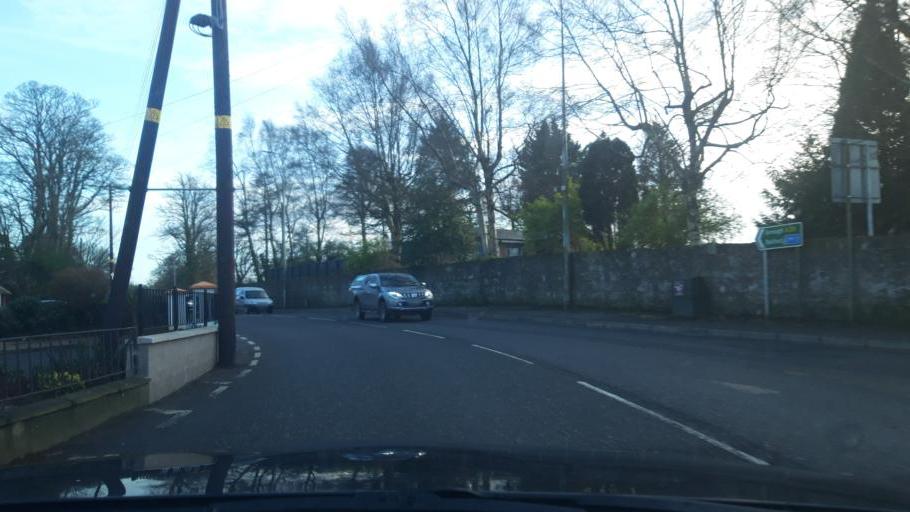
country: GB
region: Northern Ireland
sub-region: Dungannon District
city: Dungannon
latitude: 54.4985
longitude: -6.7623
